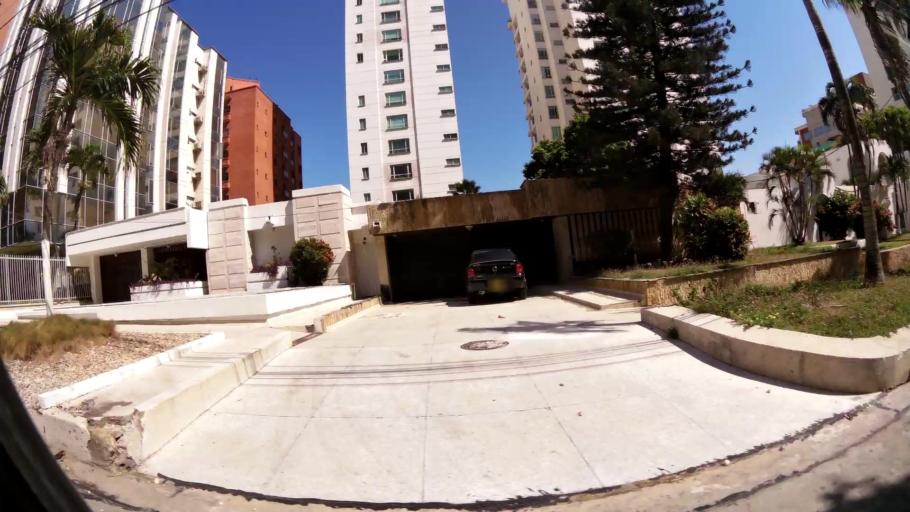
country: CO
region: Atlantico
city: Barranquilla
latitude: 11.0079
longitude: -74.8090
